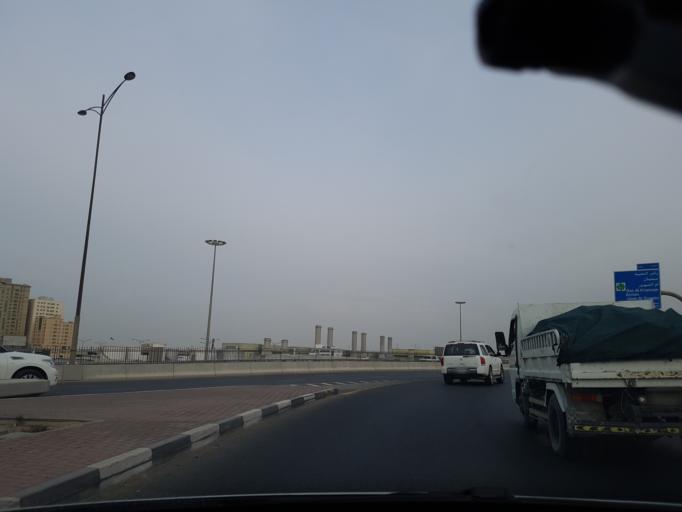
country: AE
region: Ajman
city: Ajman
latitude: 25.3737
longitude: 55.4537
